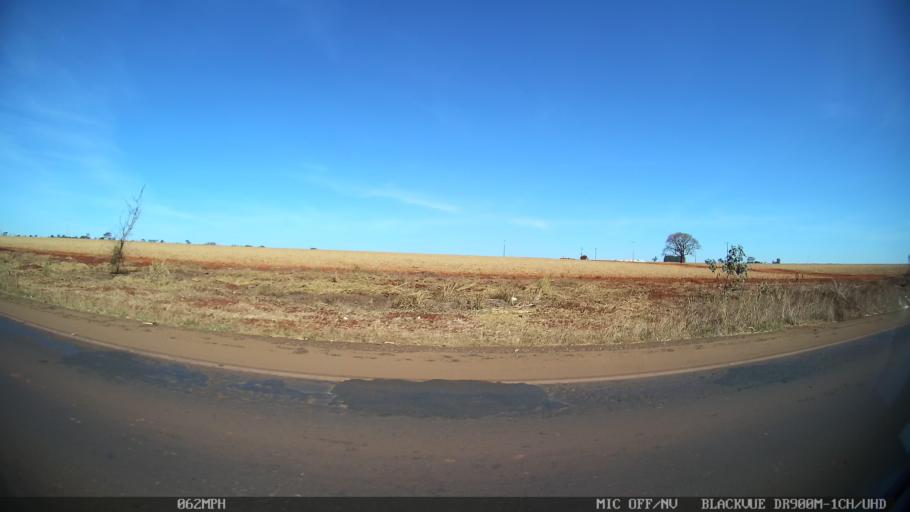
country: BR
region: Sao Paulo
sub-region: Sao Joaquim Da Barra
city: Sao Joaquim da Barra
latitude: -20.5200
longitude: -47.8669
